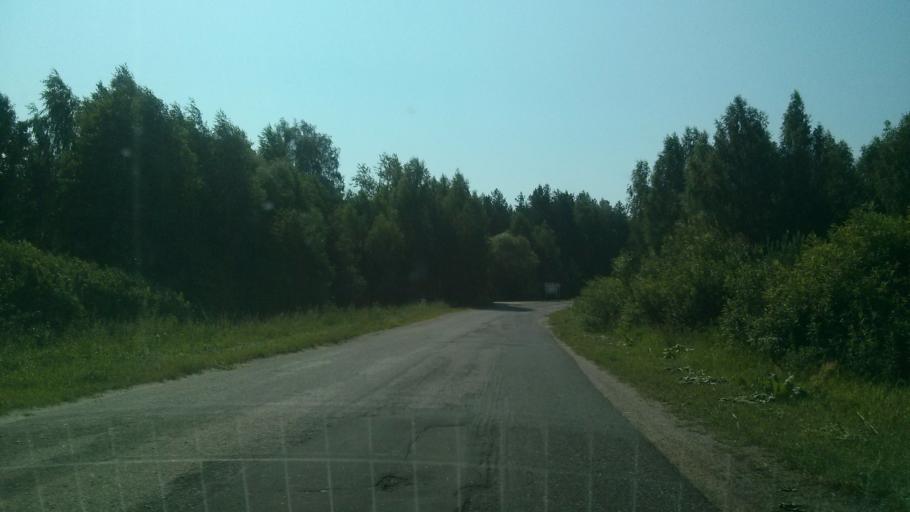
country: RU
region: Vladimir
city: Murom
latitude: 55.4567
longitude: 41.9818
